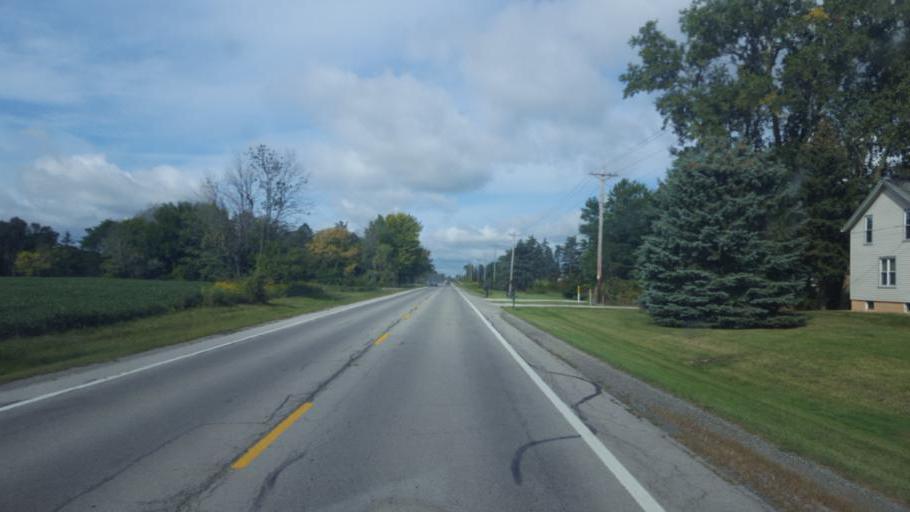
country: US
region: Ohio
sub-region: Lorain County
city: Wellington
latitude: 41.1688
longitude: -82.1452
